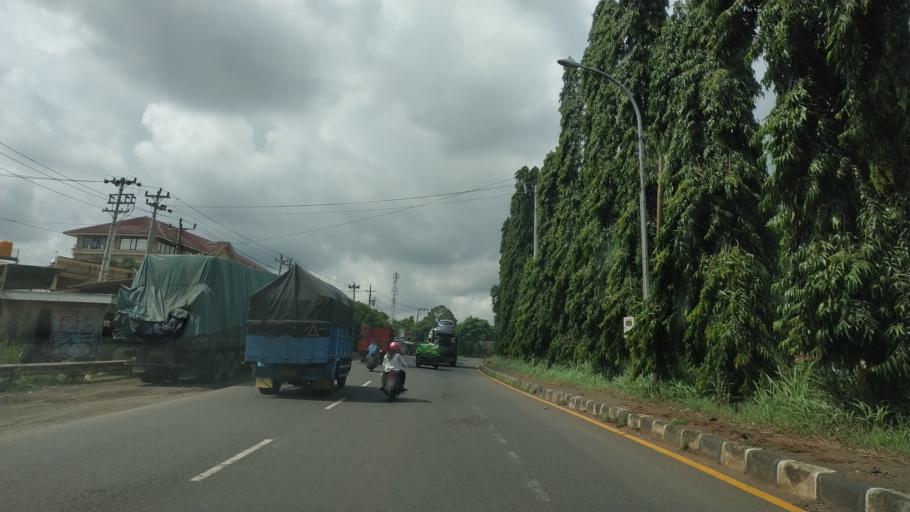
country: ID
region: Central Java
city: Pekalongan
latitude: -6.9285
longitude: 109.7635
